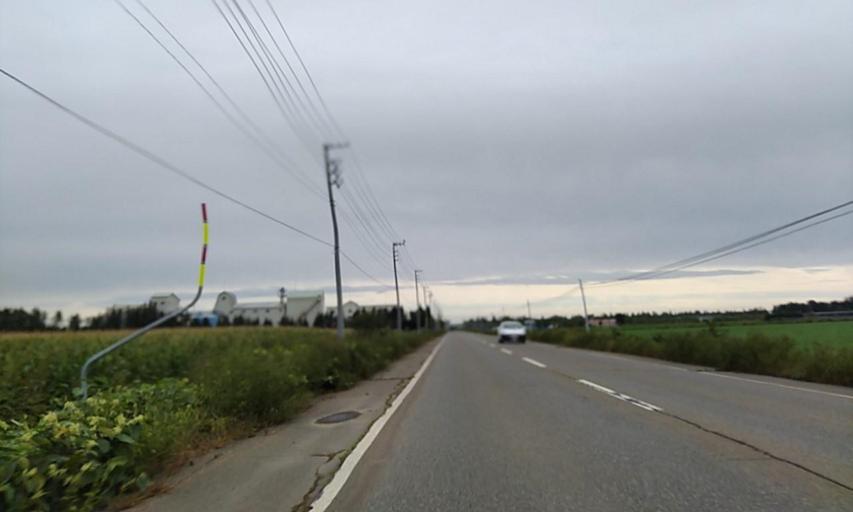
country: JP
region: Hokkaido
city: Obihiro
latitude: 42.6848
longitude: 143.1397
